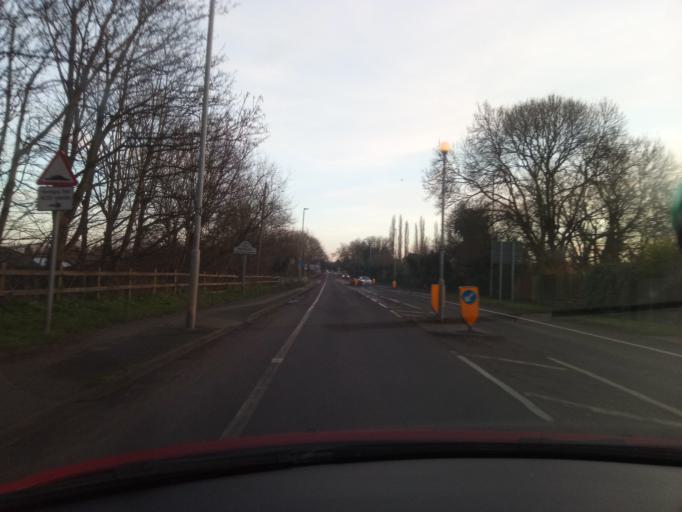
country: GB
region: England
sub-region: Leicestershire
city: Mountsorrel
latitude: 52.7228
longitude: -1.1325
